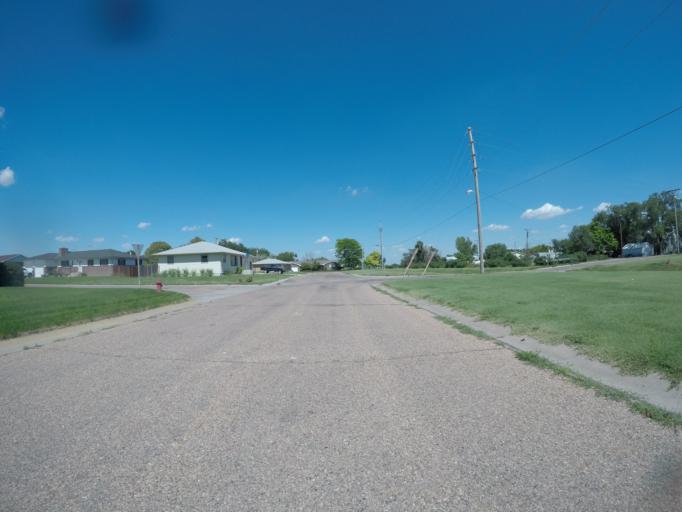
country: US
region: Kansas
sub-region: Sheridan County
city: Hoxie
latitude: 39.3587
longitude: -100.4351
